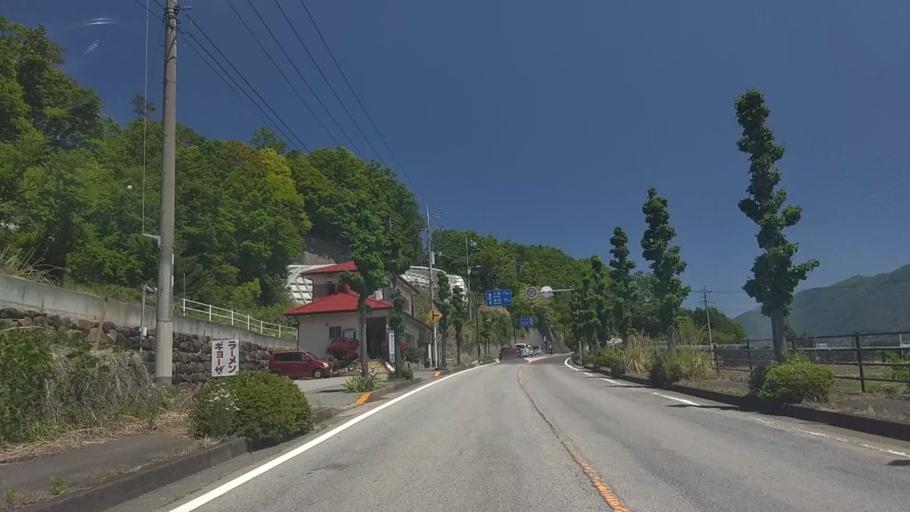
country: JP
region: Yamanashi
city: Nirasaki
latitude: 35.8000
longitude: 138.4251
